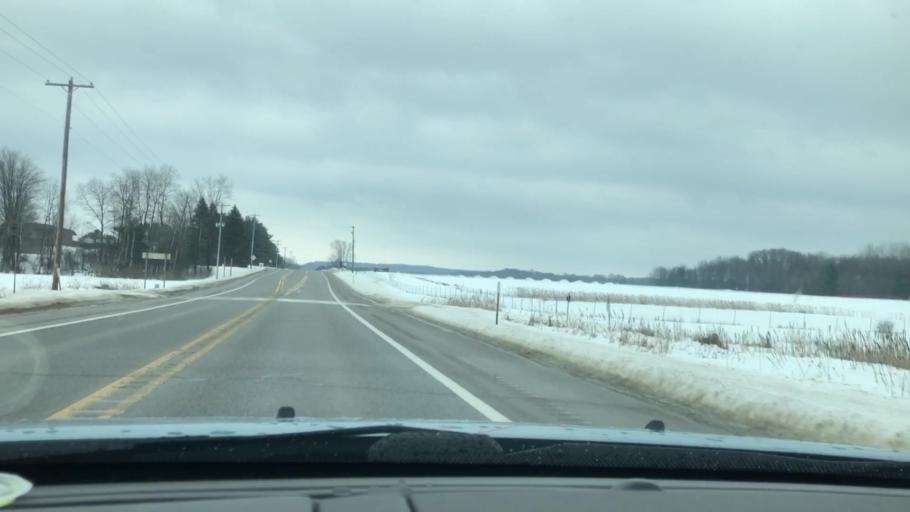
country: US
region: Michigan
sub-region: Charlevoix County
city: East Jordan
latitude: 45.1325
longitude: -85.1167
